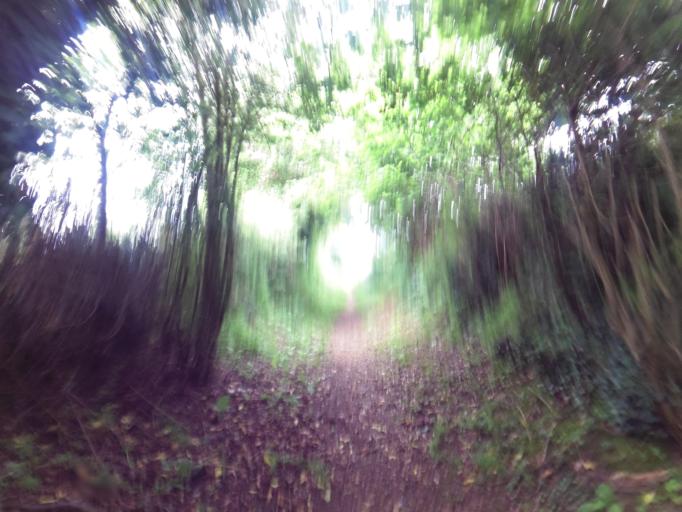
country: FR
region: Brittany
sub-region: Departement du Morbihan
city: Molac
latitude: 47.7683
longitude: -2.4298
